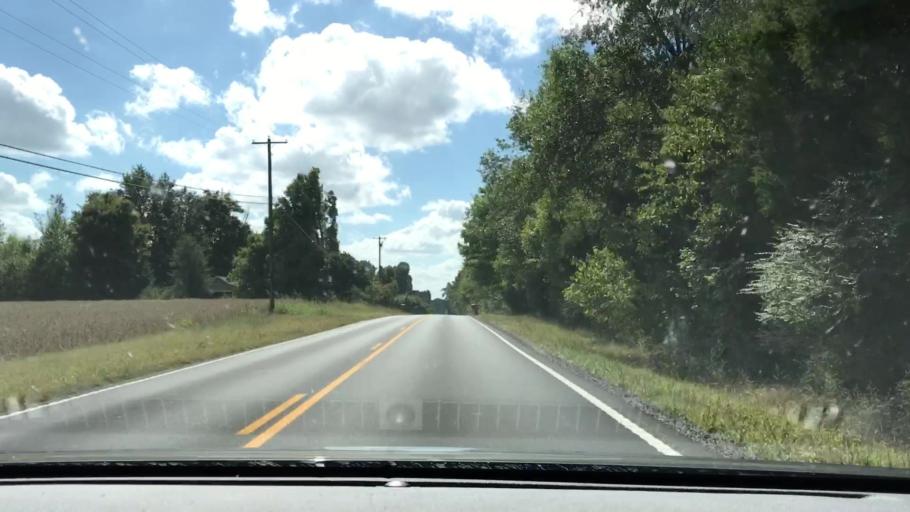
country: US
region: Kentucky
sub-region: Graves County
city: Mayfield
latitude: 36.7962
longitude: -88.5955
